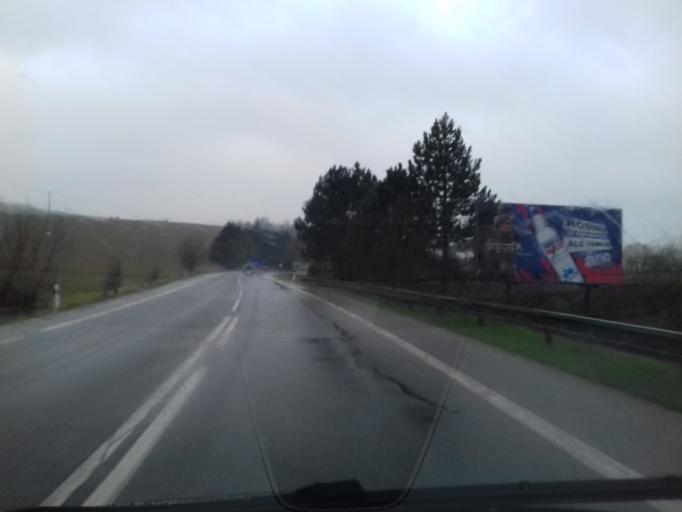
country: SK
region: Presovsky
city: Stara L'ubovna
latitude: 49.2852
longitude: 20.7372
